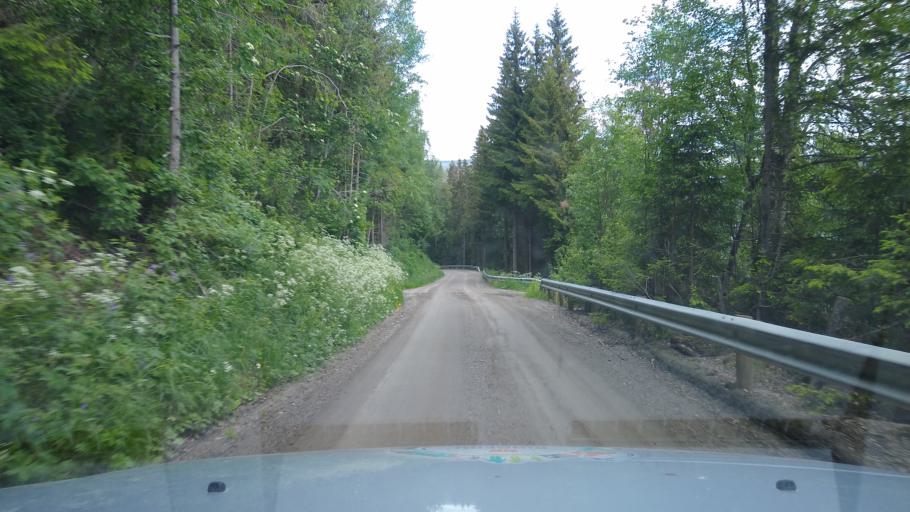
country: NO
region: Oppland
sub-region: Ringebu
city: Ringebu
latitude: 61.5026
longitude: 10.1389
